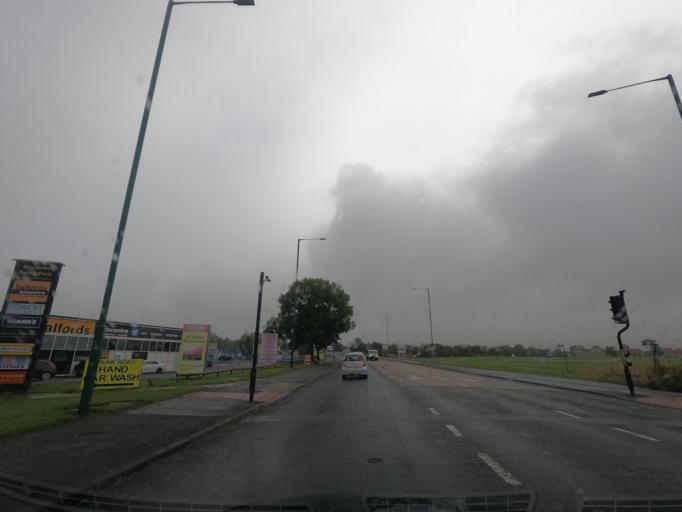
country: GB
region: England
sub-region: Redcar and Cleveland
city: South Bank
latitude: 54.5688
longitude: -1.1761
